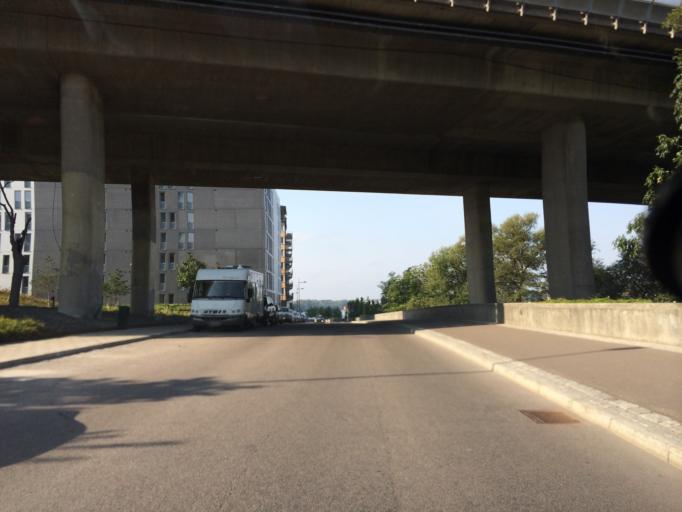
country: SE
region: Stockholm
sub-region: Solna Kommun
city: Solna
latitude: 59.3404
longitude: 18.0118
